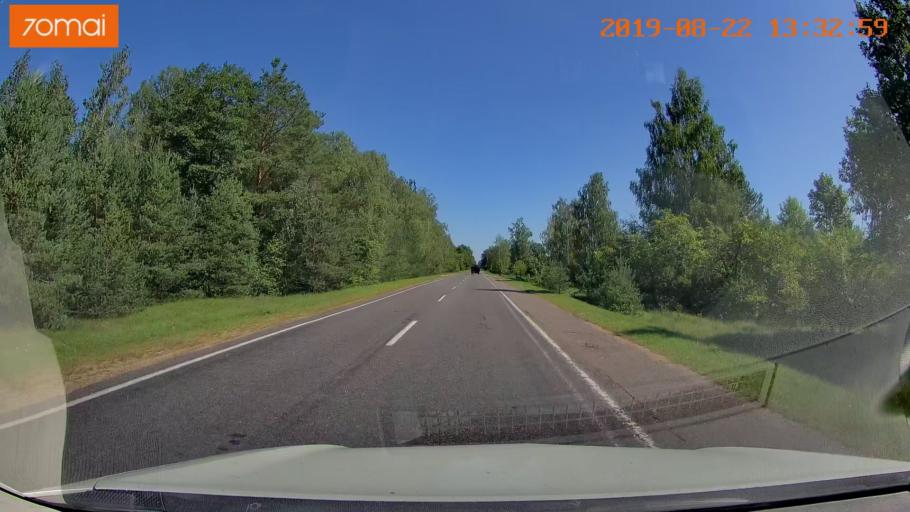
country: BY
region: Minsk
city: Staryya Darohi
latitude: 53.2169
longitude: 28.2170
